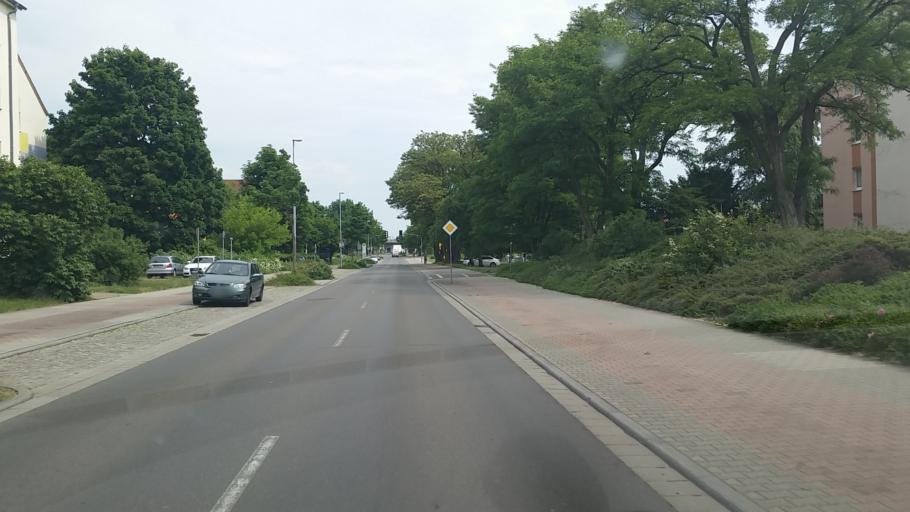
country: DE
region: Brandenburg
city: Schwarzheide
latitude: 51.4744
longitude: 13.8629
